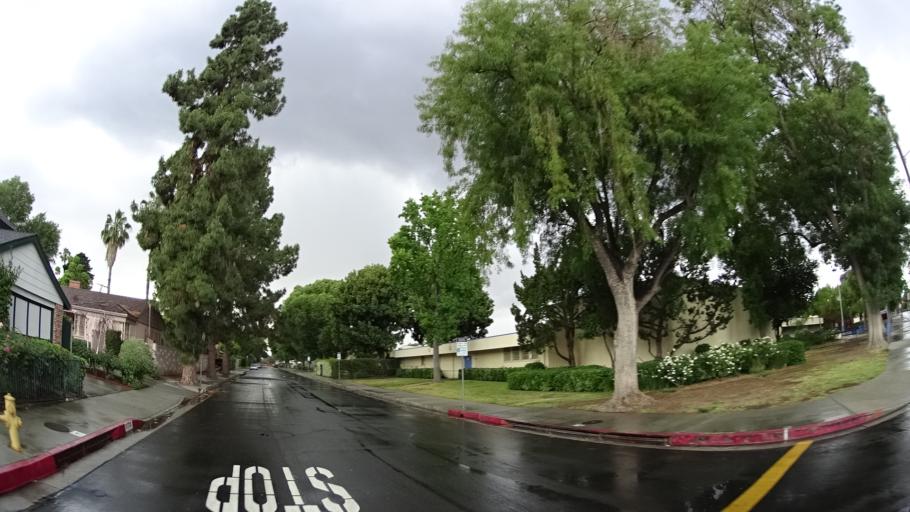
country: US
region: California
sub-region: Los Angeles County
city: Sherman Oaks
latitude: 34.1622
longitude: -118.4269
